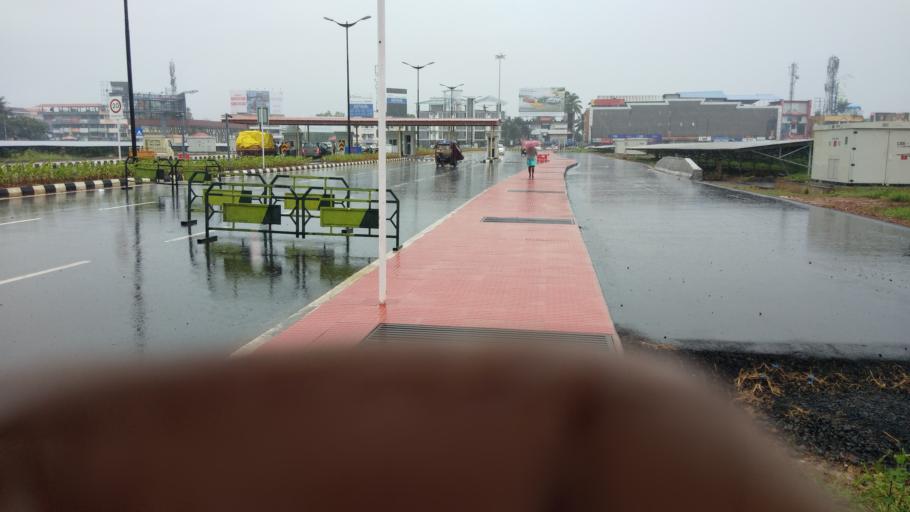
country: IN
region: Kerala
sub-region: Ernakulam
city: Angamali
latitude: 10.1592
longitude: 76.3876
